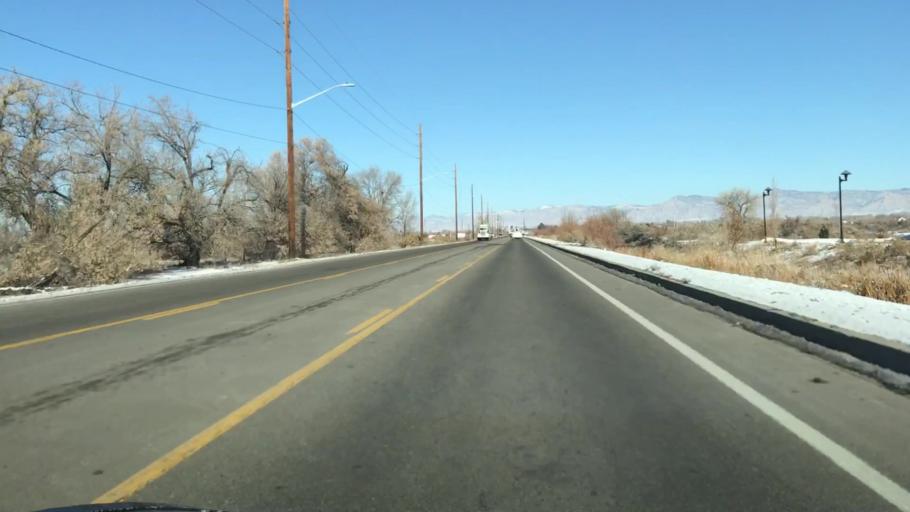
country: US
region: Colorado
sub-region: Mesa County
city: Redlands
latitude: 39.1006
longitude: -108.6079
